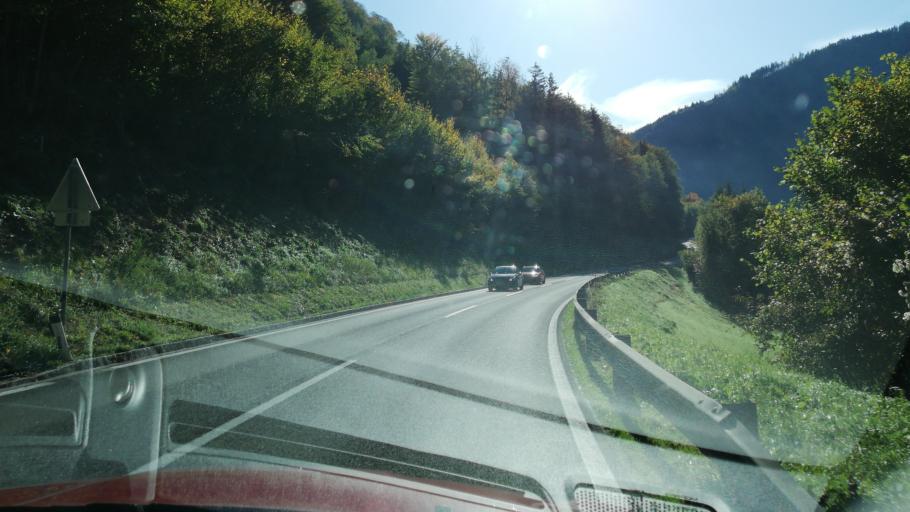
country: AT
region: Upper Austria
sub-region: Politischer Bezirk Steyr-Land
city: Weyer
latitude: 47.8601
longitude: 14.6149
